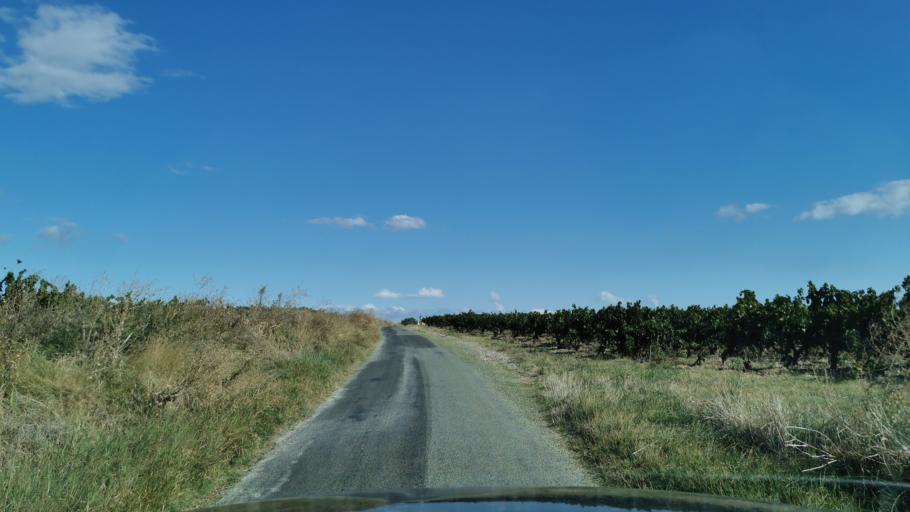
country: FR
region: Languedoc-Roussillon
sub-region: Departement de l'Aude
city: Ginestas
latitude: 43.2659
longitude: 2.8435
